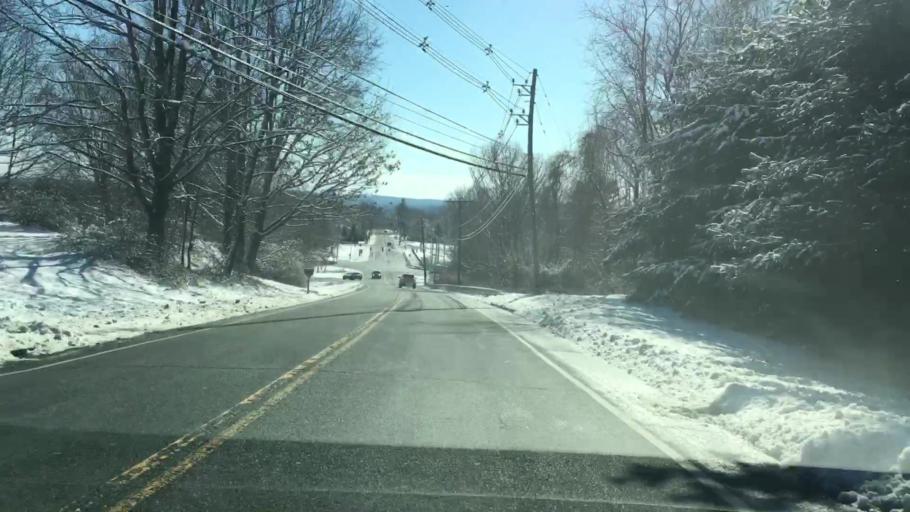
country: US
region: Connecticut
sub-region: Litchfield County
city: Oakville
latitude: 41.6097
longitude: -73.0923
